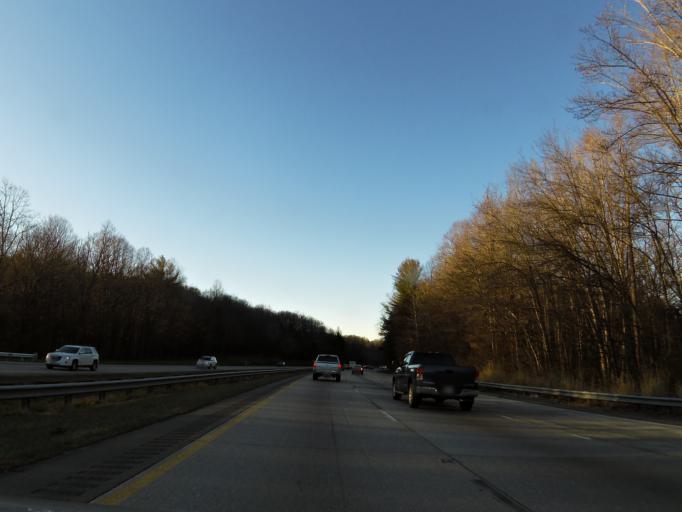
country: US
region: North Carolina
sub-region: Henderson County
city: Mountain Home
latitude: 35.3810
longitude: -82.4844
